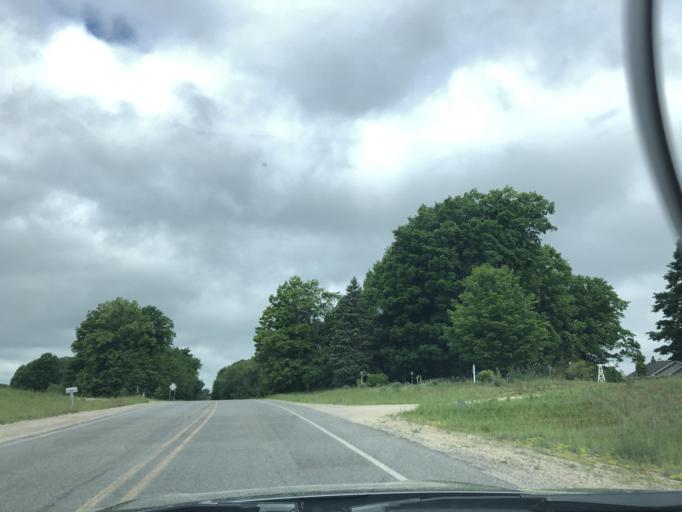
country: US
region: Michigan
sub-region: Missaukee County
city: Lake City
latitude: 44.4535
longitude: -85.2011
